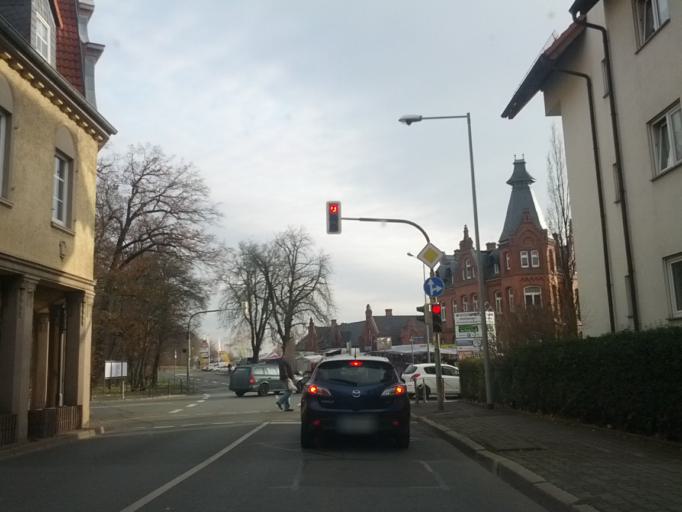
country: DE
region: Thuringia
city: Gotha
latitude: 50.9402
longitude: 10.6997
